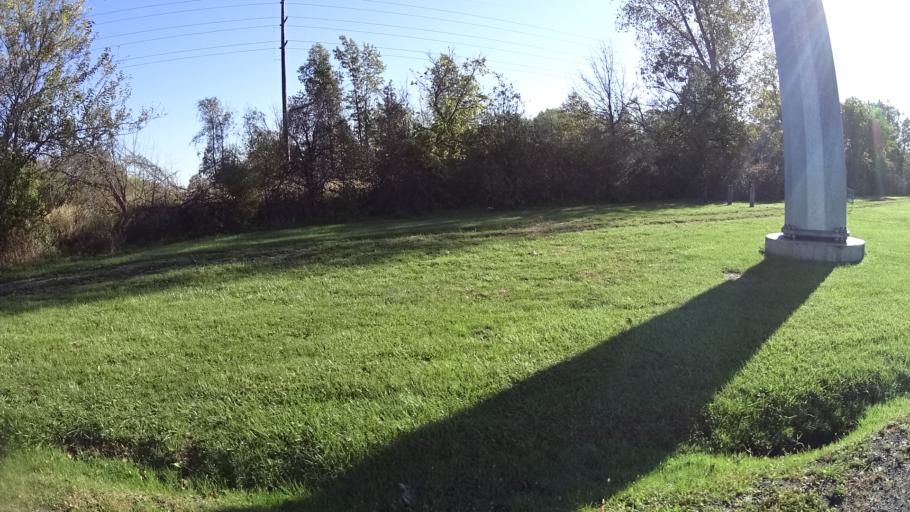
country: US
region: Ohio
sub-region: Lorain County
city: Lorain
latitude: 41.4410
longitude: -82.1529
